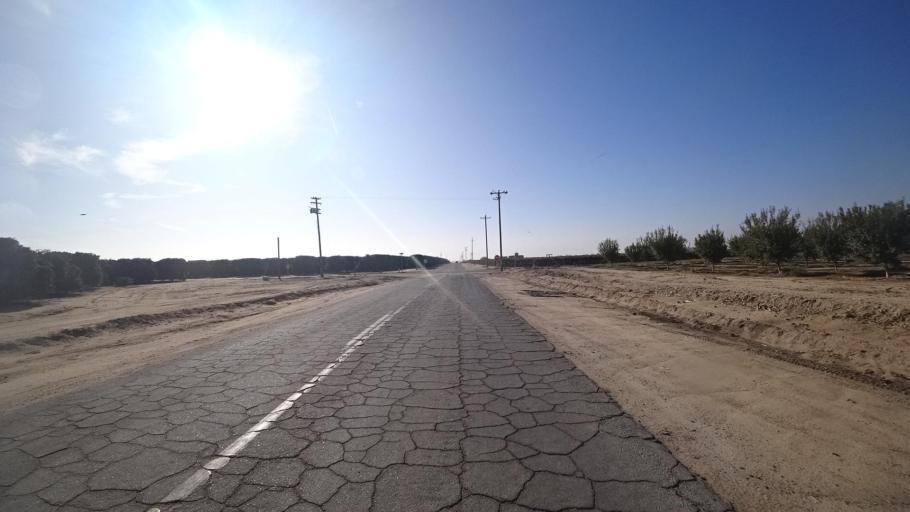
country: US
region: California
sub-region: Kern County
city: Lamont
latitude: 35.3259
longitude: -118.8966
